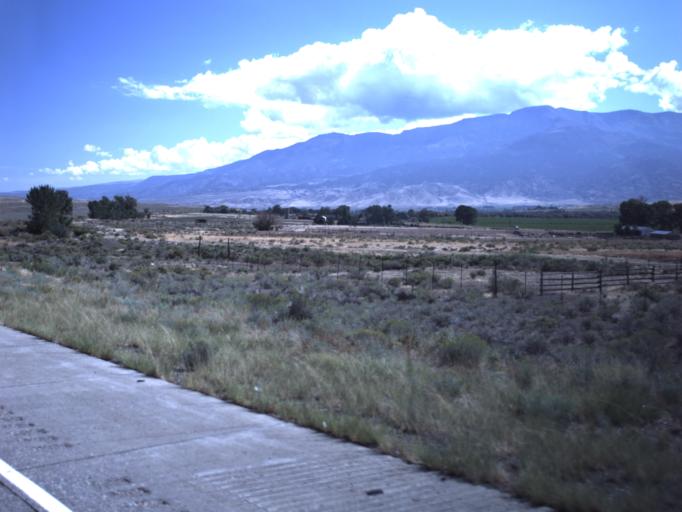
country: US
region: Utah
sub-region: Sevier County
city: Monroe
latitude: 38.6537
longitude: -112.2094
